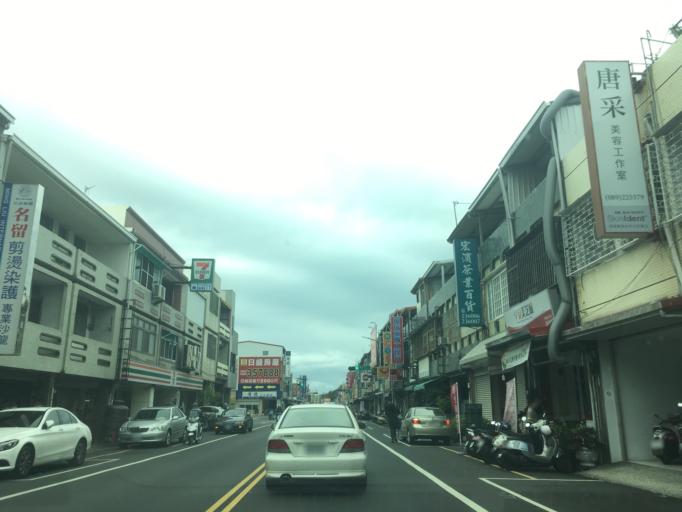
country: TW
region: Taiwan
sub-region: Taitung
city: Taitung
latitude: 22.7639
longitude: 121.1357
